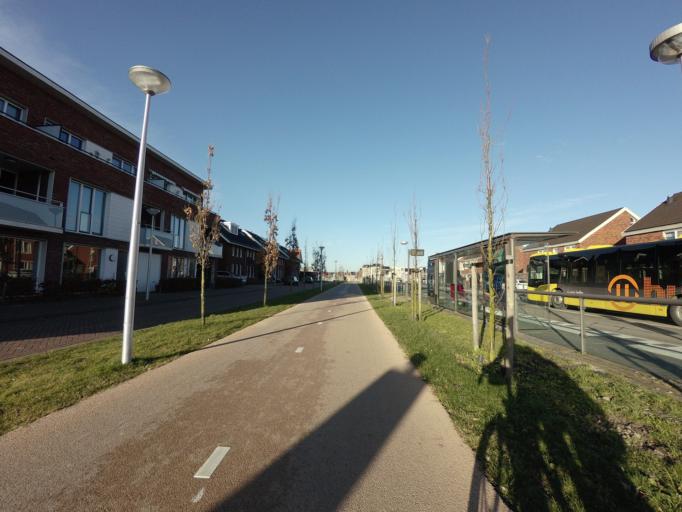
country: NL
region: Utrecht
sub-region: Stichtse Vecht
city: Spechtenkamp
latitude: 52.0892
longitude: 5.0131
